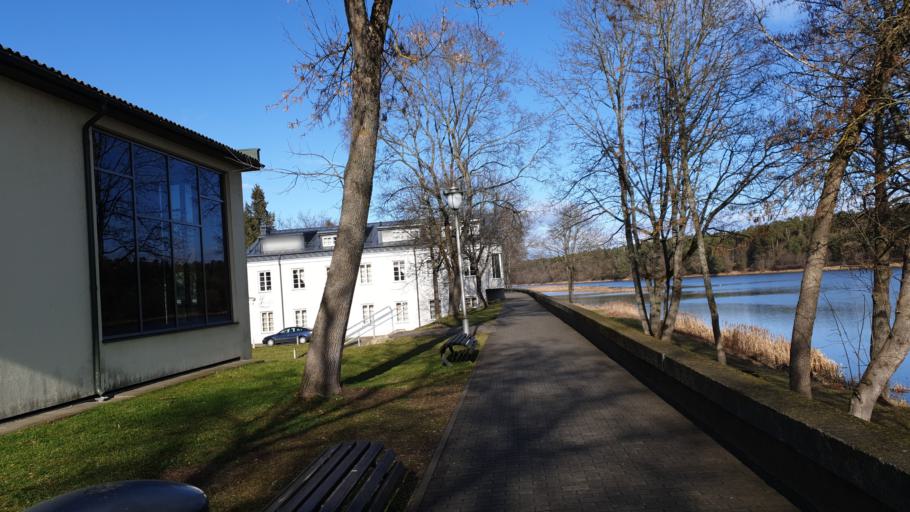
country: LT
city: Birstonas
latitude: 54.6005
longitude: 24.0359
